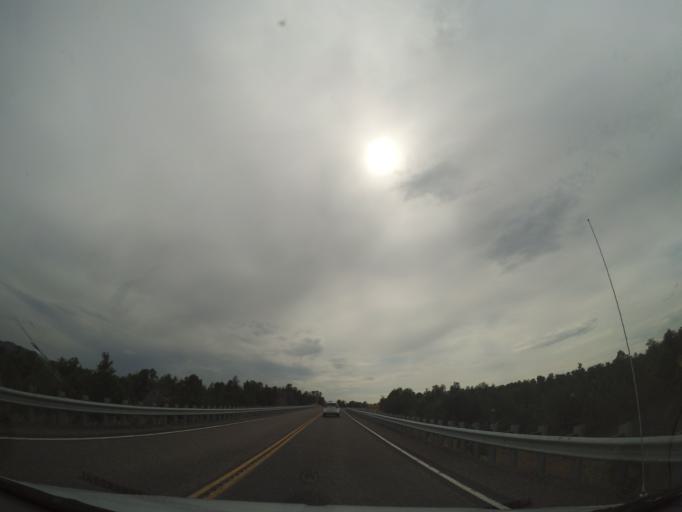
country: US
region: Utah
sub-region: Kane County
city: Kanab
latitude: 37.2221
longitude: -112.6927
